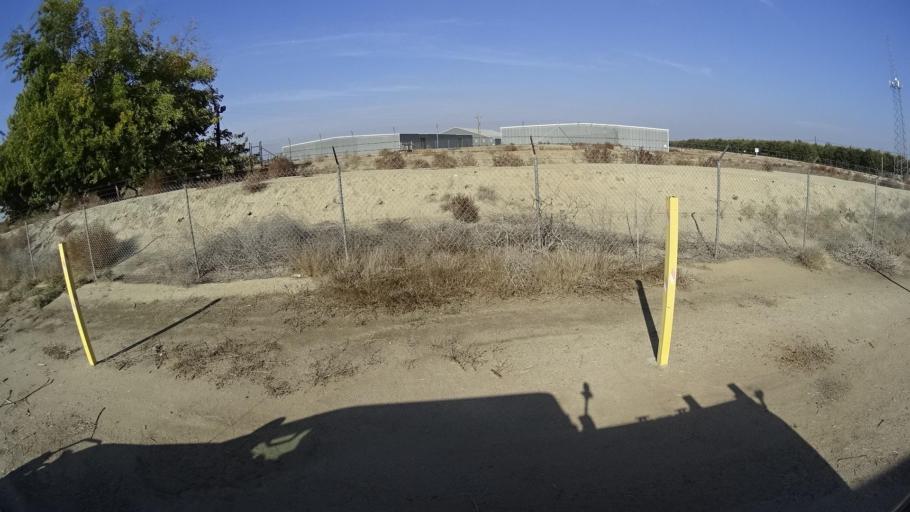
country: US
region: California
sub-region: Kern County
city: McFarland
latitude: 35.6311
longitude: -119.2079
